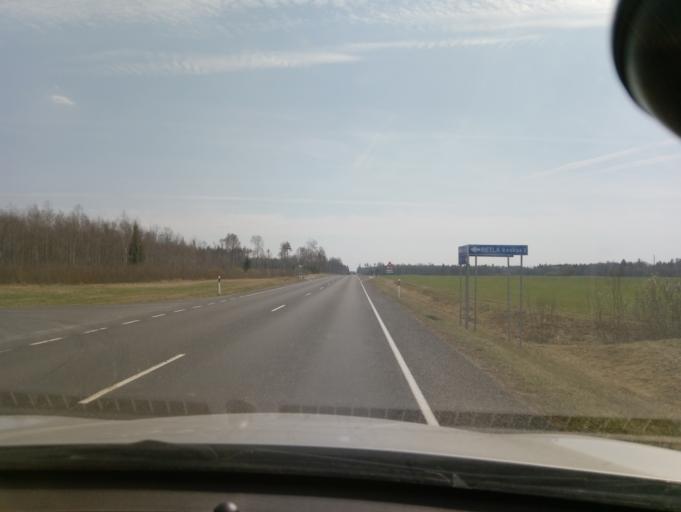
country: EE
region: Viljandimaa
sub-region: Vohma linn
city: Vohma
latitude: 58.7282
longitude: 25.5971
